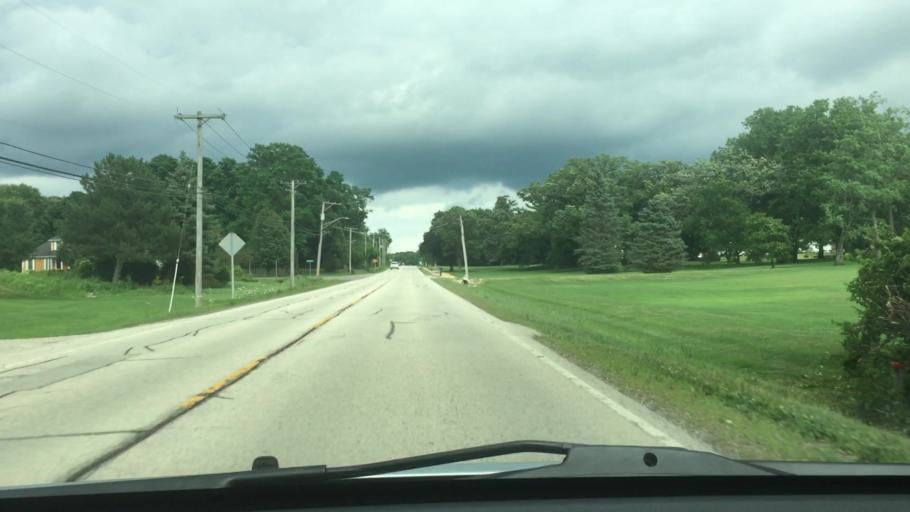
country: US
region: Illinois
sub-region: McHenry County
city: Prairie Grove
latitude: 42.2847
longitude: -88.2991
